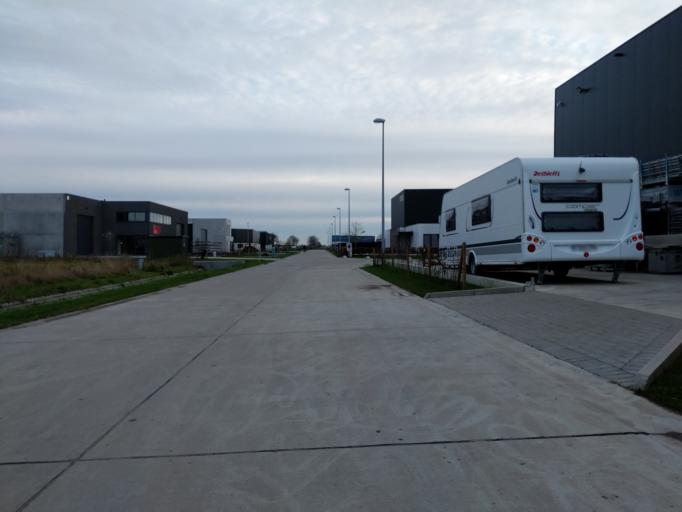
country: BE
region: Flanders
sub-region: Provincie West-Vlaanderen
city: Ruiselede
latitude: 51.0395
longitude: 3.4026
